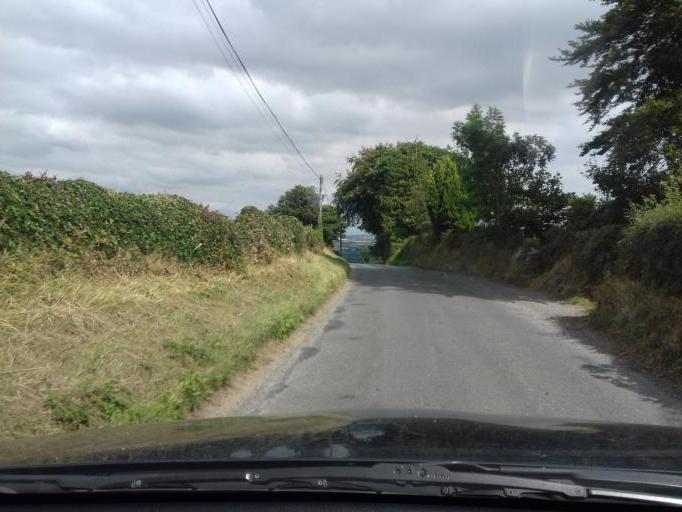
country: IE
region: Leinster
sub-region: Loch Garman
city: Bunclody
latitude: 52.6454
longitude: -6.6975
